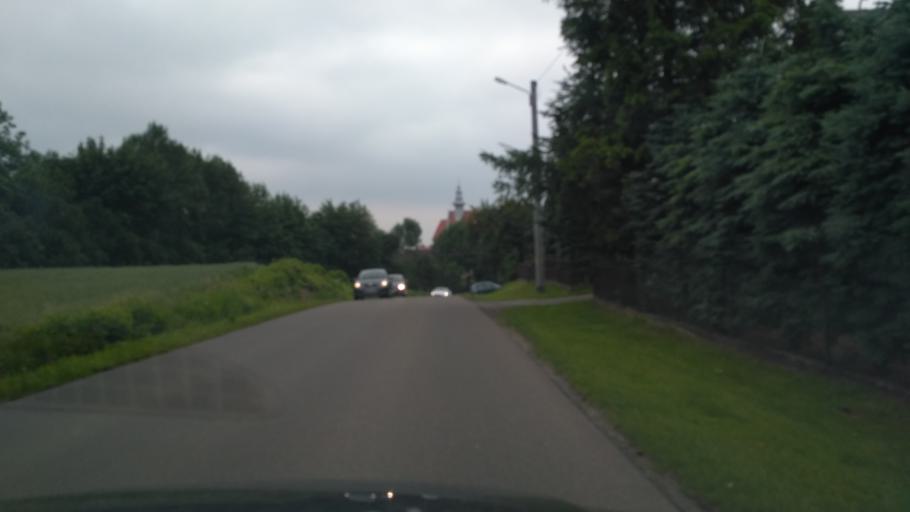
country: PL
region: Subcarpathian Voivodeship
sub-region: Powiat ropczycko-sedziszowski
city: Sedziszow Malopolski
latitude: 50.0509
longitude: 21.6882
